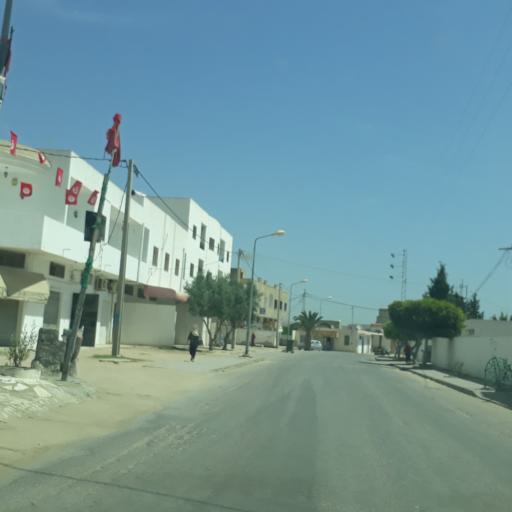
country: TN
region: Safaqis
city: Al Qarmadah
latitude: 34.8171
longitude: 10.7743
